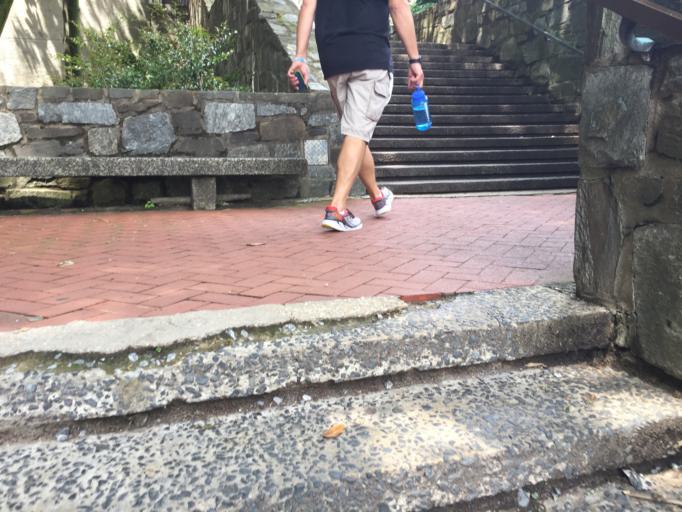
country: US
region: Washington, D.C.
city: Washington, D.C.
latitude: 38.9067
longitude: -77.0719
